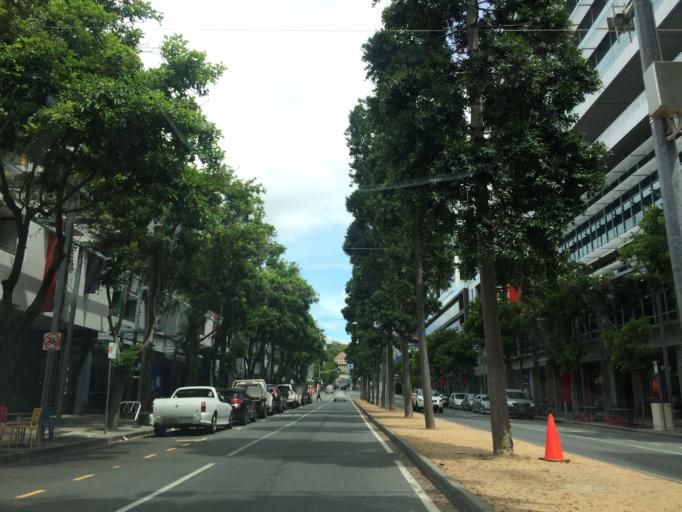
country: AU
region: Queensland
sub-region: Brisbane
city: South Brisbane
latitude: -27.4796
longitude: 153.0223
